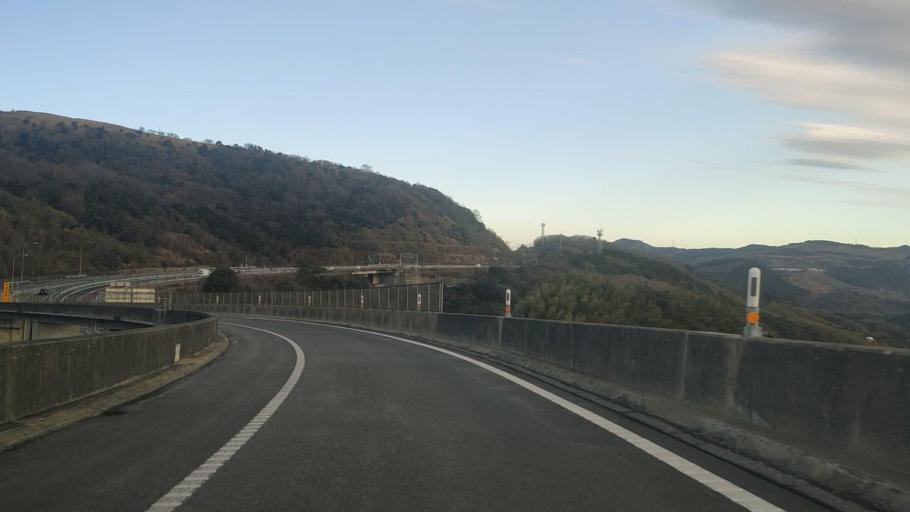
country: JP
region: Oita
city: Hiji
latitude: 33.3529
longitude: 131.4465
